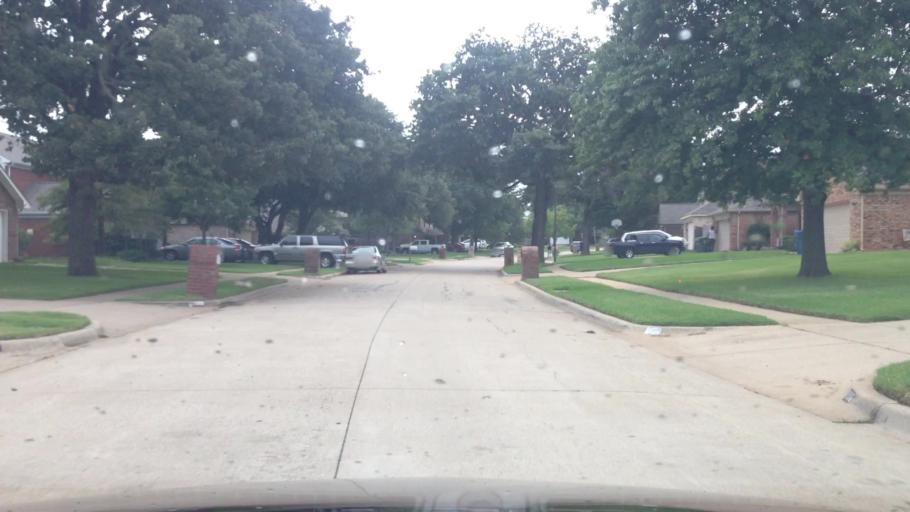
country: US
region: Texas
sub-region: Denton County
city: Flower Mound
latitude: 33.0245
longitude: -97.0512
